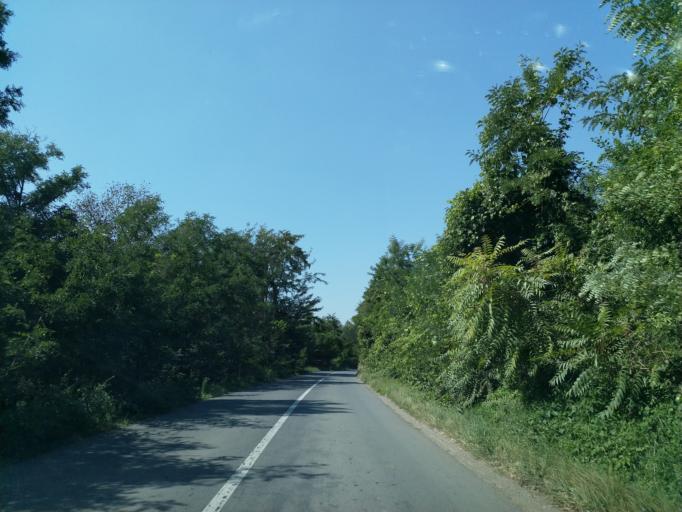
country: RS
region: Central Serbia
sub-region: Rasinski Okrug
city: Trstenik
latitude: 43.6207
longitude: 21.1650
